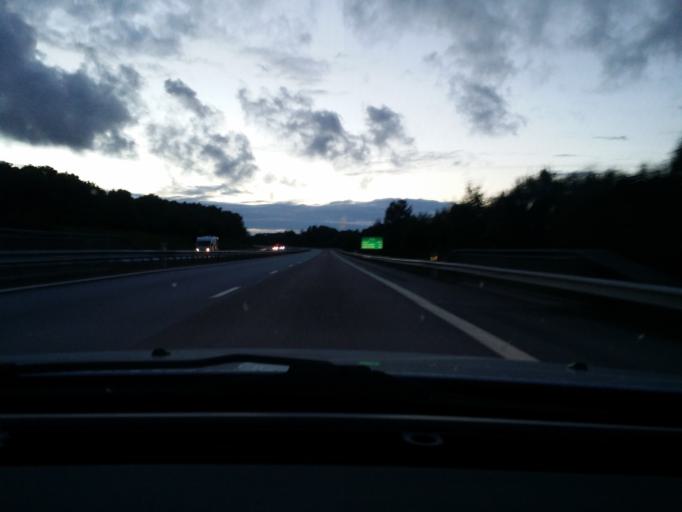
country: SE
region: Uppsala
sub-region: Habo Kommun
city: Balsta
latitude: 59.5881
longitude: 17.5026
